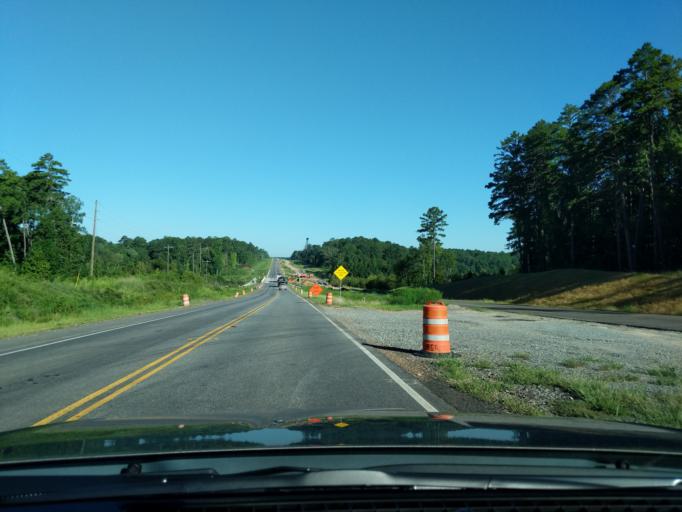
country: US
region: Georgia
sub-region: McDuffie County
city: Thomson
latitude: 33.5799
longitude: -82.5282
